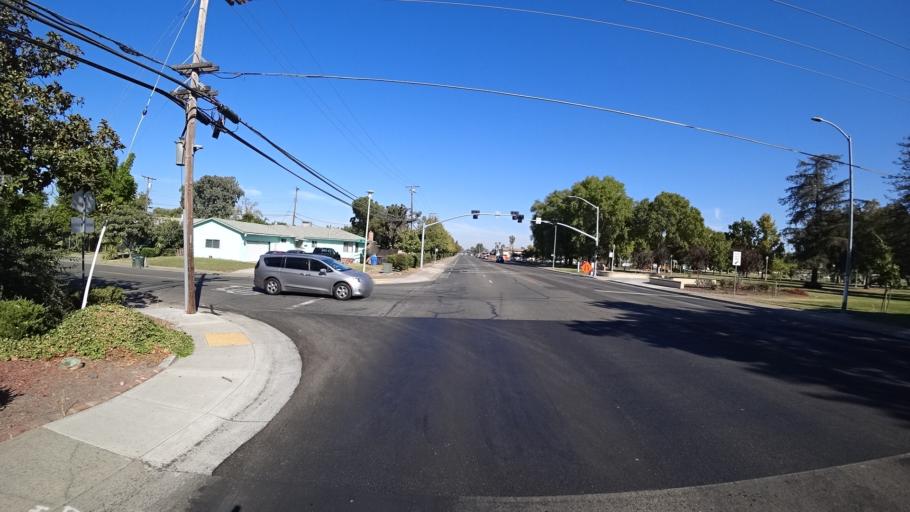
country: US
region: California
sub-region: Sacramento County
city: Parkway
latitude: 38.5029
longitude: -121.4829
